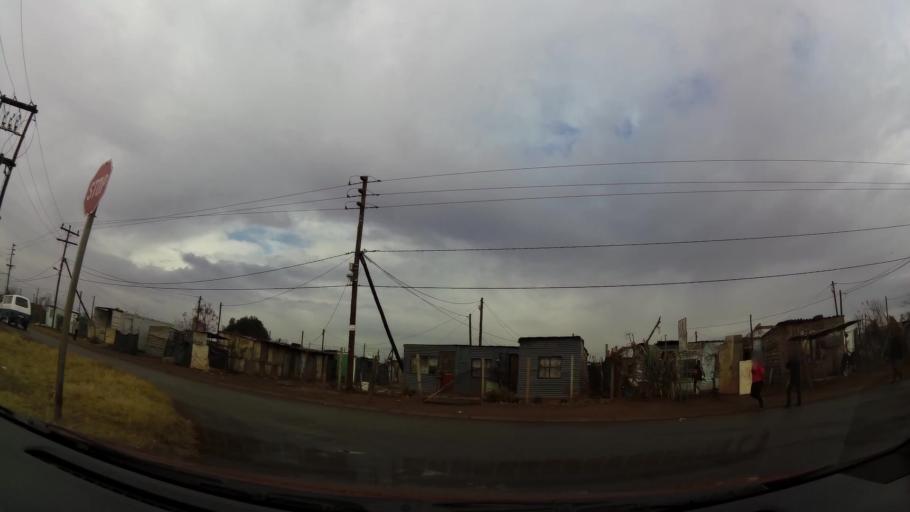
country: ZA
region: Gauteng
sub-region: City of Johannesburg Metropolitan Municipality
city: Soweto
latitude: -26.2902
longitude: 27.8399
